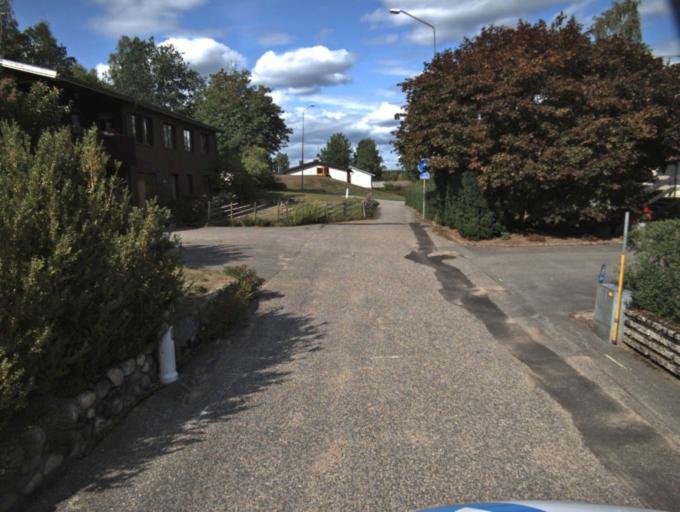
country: SE
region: Vaestra Goetaland
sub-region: Ulricehamns Kommun
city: Ulricehamn
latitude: 57.6816
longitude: 13.3754
